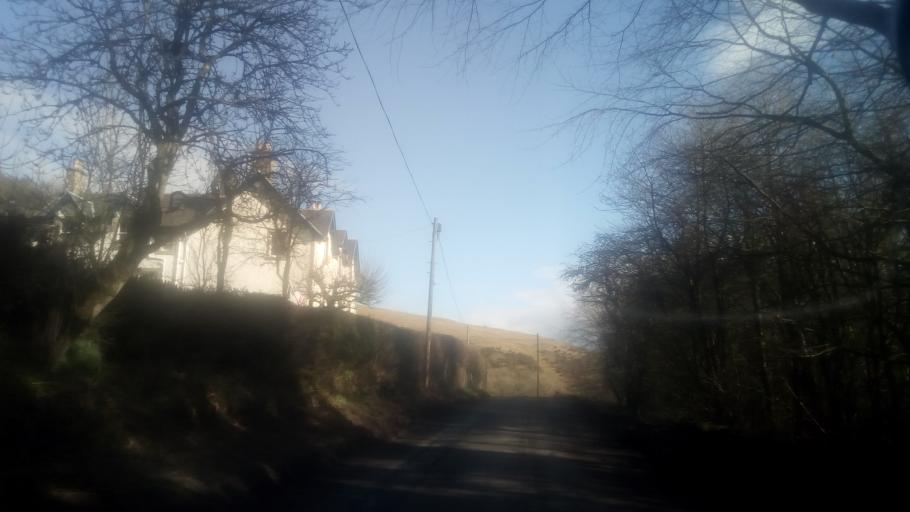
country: GB
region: Scotland
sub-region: The Scottish Borders
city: Hawick
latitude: 55.4173
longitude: -2.8583
